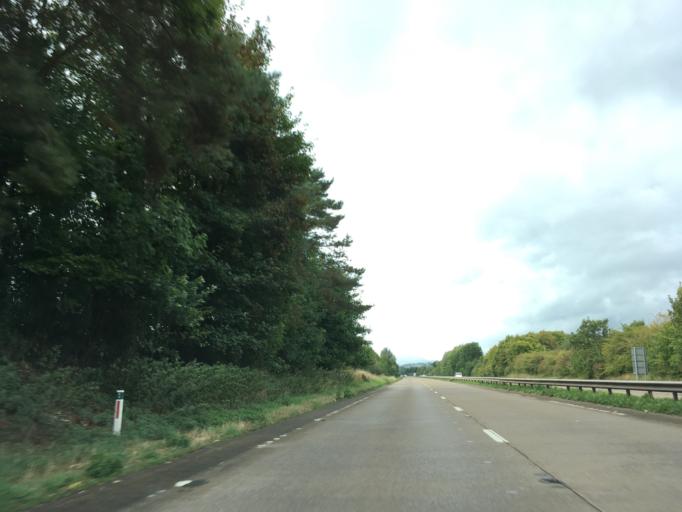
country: GB
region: Wales
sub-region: Monmouthshire
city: Llanarth
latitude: 51.7769
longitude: -2.8876
